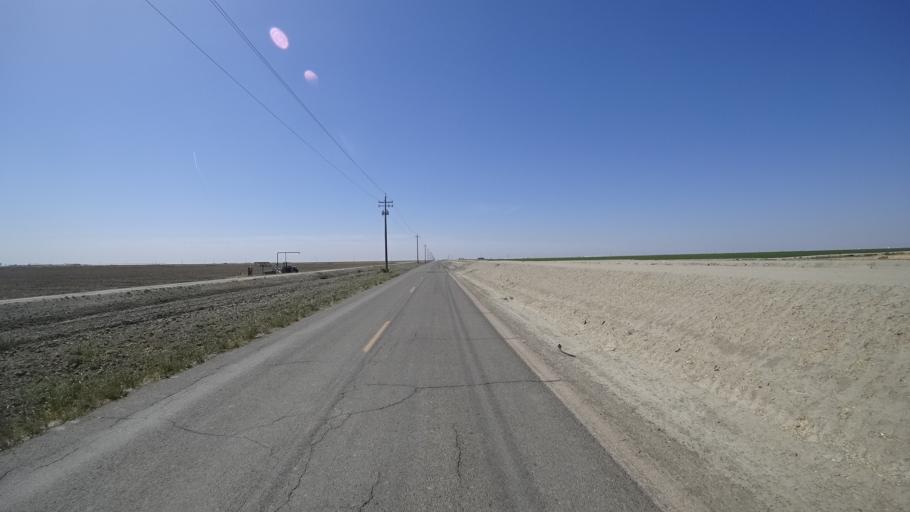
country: US
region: California
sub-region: Kings County
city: Corcoran
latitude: 36.0007
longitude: -119.5362
